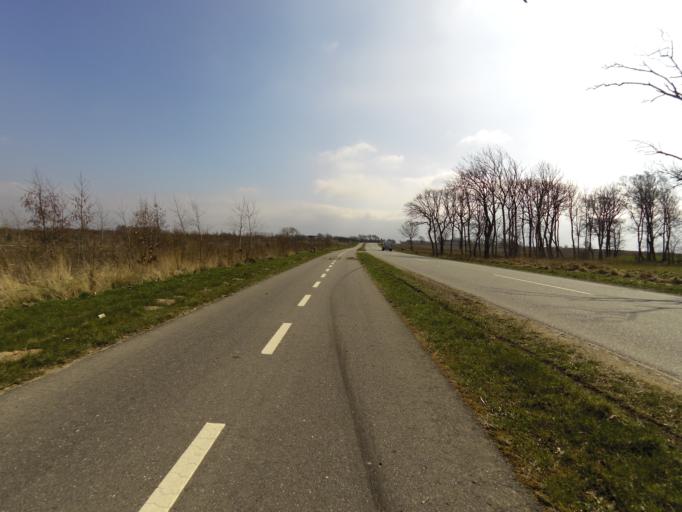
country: DK
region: Central Jutland
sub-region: Struer Kommune
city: Struer
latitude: 56.4469
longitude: 8.6240
